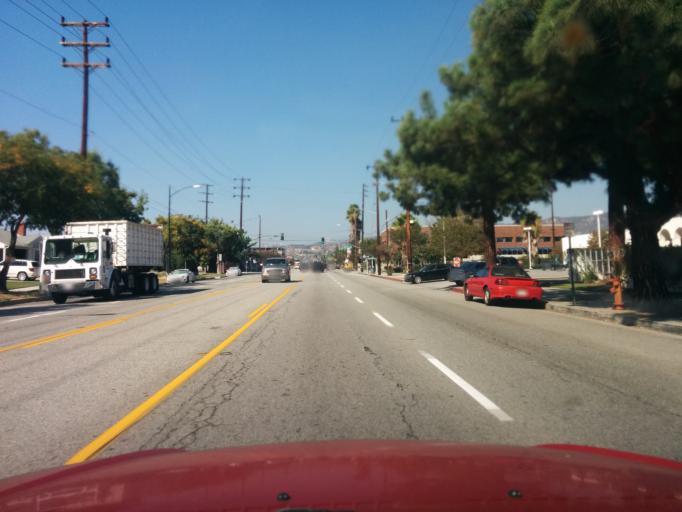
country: US
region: California
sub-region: Los Angeles County
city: North Hollywood
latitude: 34.1871
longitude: -118.3493
